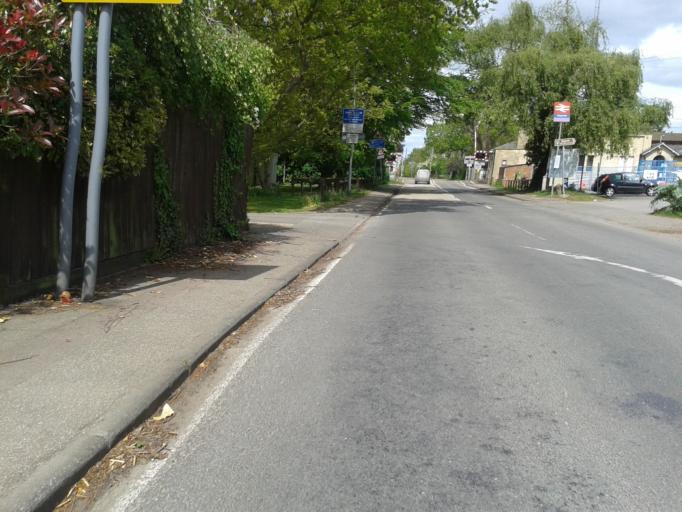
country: GB
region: England
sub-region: Cambridgeshire
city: Meldreth
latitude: 52.1135
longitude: 0.0316
